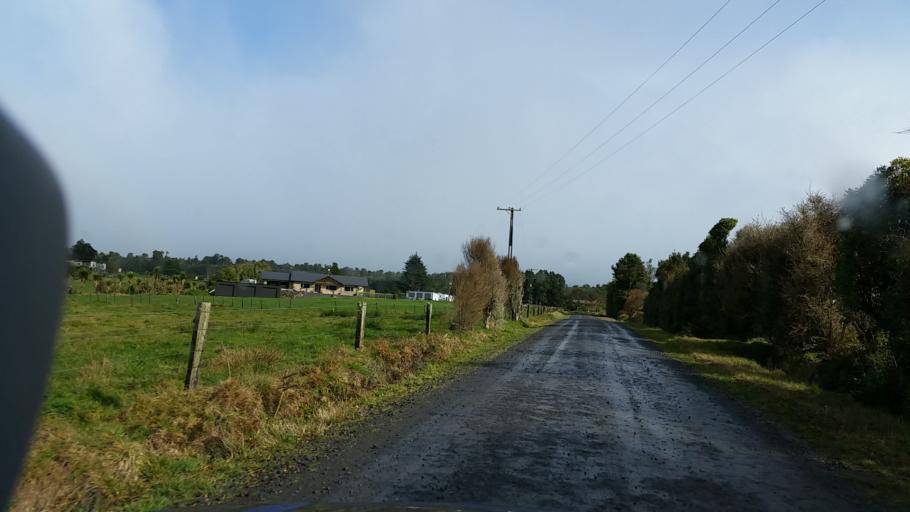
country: NZ
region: Taranaki
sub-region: South Taranaki District
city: Eltham
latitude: -39.2868
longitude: 174.1856
